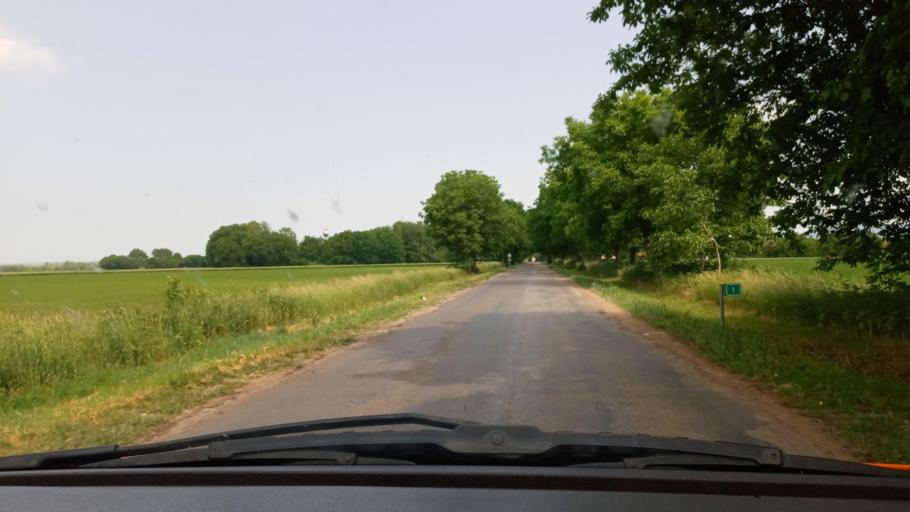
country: HU
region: Baranya
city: Szentlorinc
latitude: 46.0009
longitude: 18.0374
